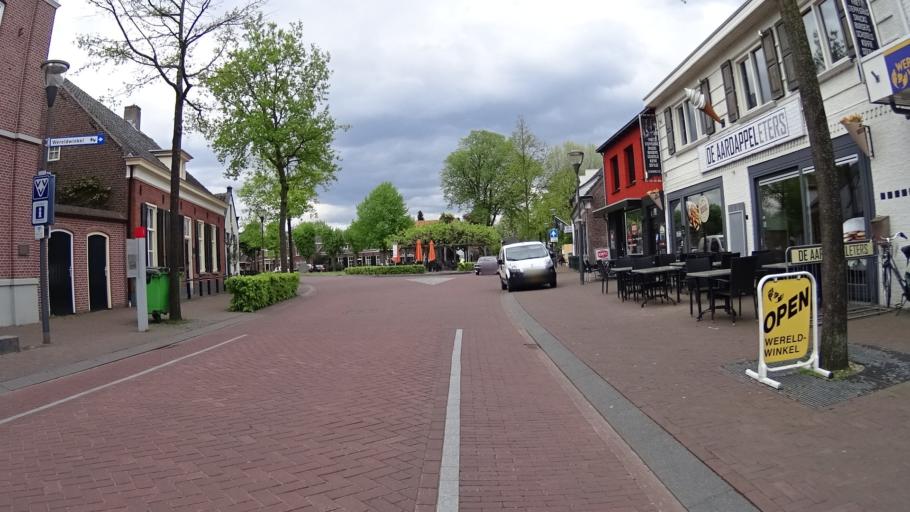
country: NL
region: North Brabant
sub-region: Gemeente Nuenen, Gerwen en Nederwetten
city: Nuenen
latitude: 51.4768
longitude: 5.5510
